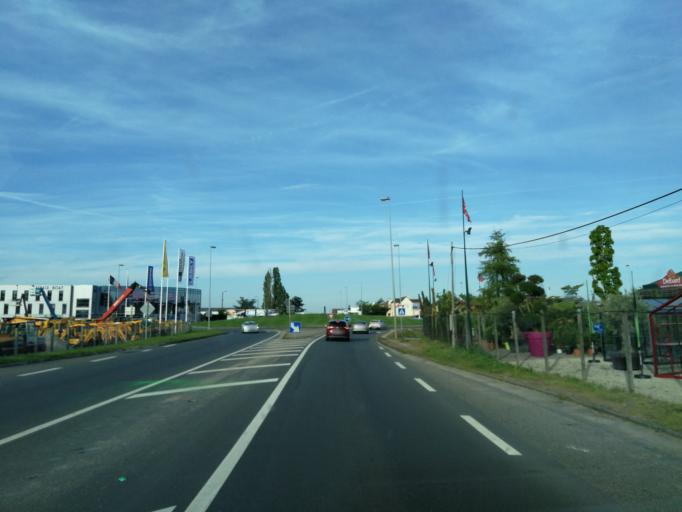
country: FR
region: Centre
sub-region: Departement d'Eure-et-Loir
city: Nogent-le-Phaye
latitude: 48.4595
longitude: 1.5680
